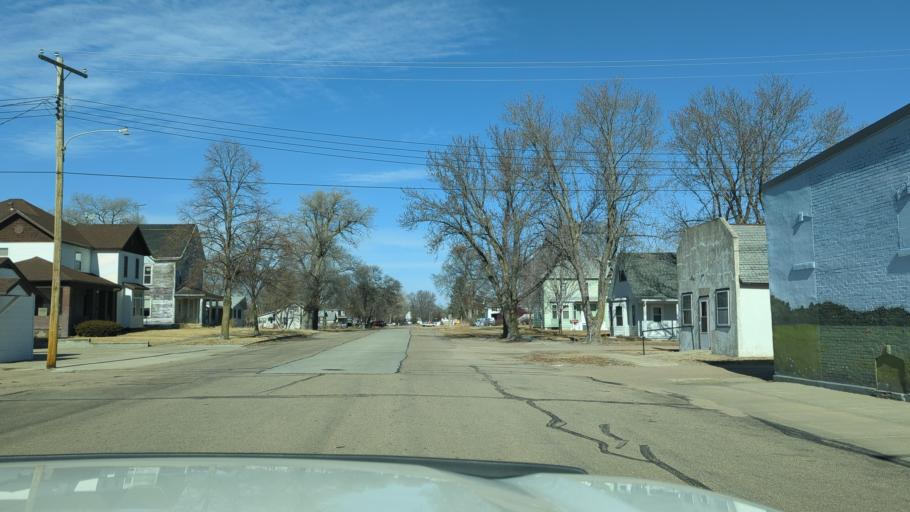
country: US
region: Nebraska
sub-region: Antelope County
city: Neligh
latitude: 42.2580
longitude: -98.3451
